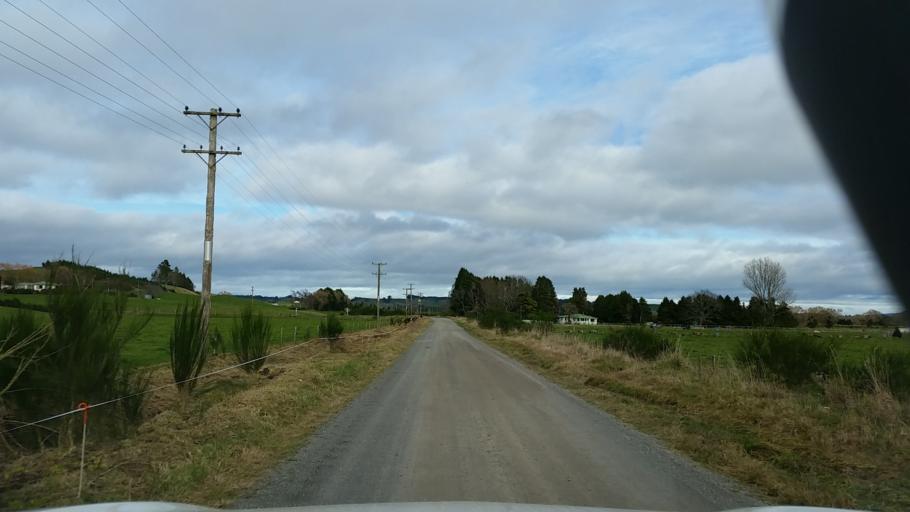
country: NZ
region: Bay of Plenty
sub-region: Whakatane District
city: Murupara
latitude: -38.2898
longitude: 176.5463
